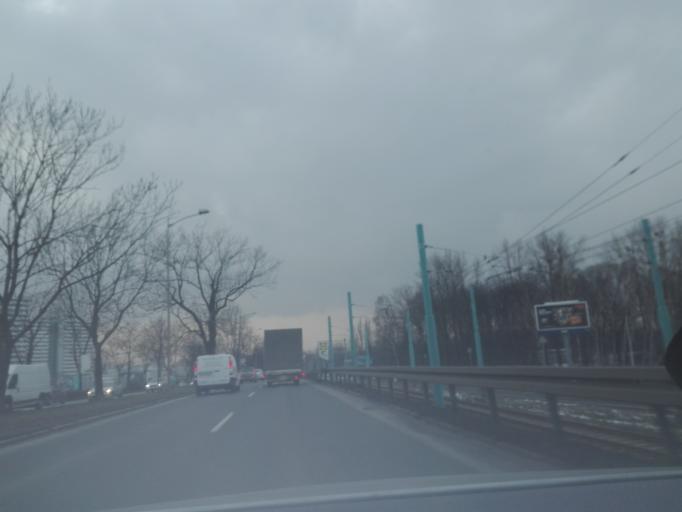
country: PL
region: Silesian Voivodeship
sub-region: Chorzow
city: Chorzow
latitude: 50.2843
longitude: 18.9728
